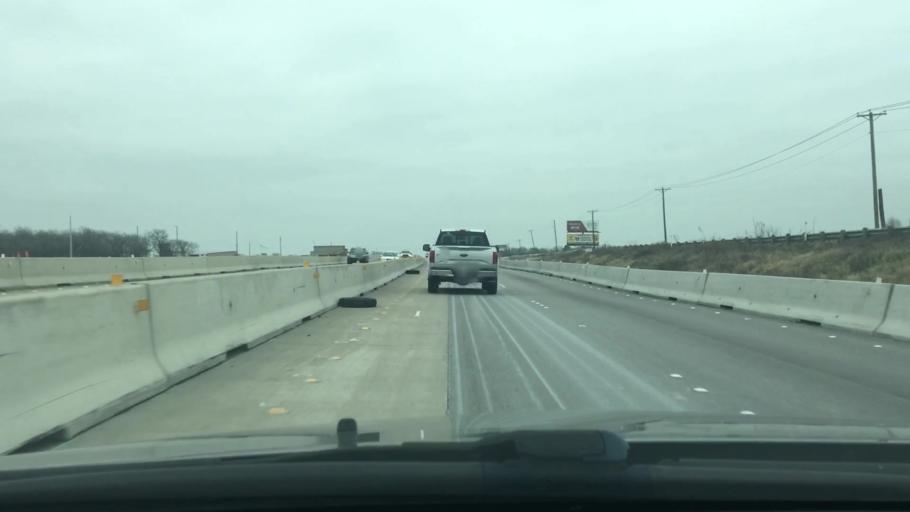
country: US
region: Texas
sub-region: Navarro County
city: Corsicana
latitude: 32.0375
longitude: -96.4457
